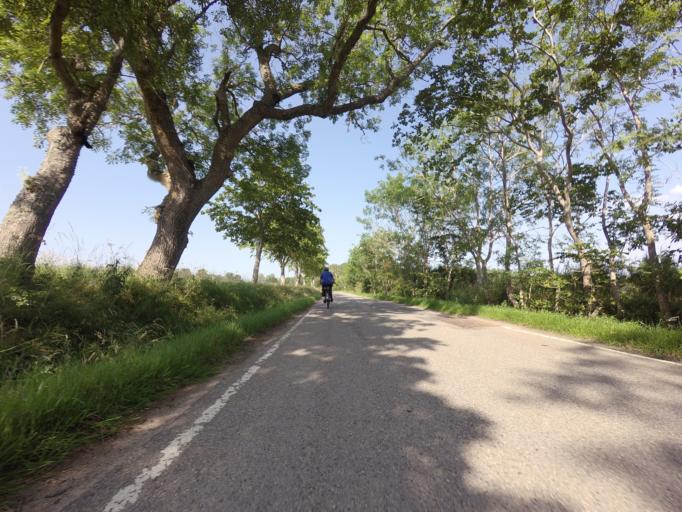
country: GB
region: Scotland
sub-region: Highland
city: Evanton
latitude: 57.6389
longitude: -4.3616
